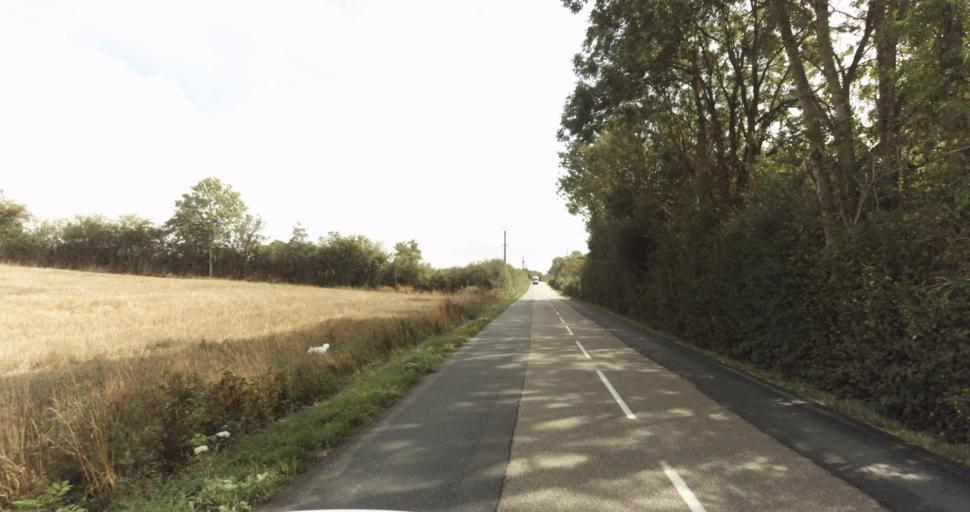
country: FR
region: Lower Normandy
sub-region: Departement de l'Orne
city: Sainte-Gauburge-Sainte-Colombe
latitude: 48.7992
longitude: 0.4003
